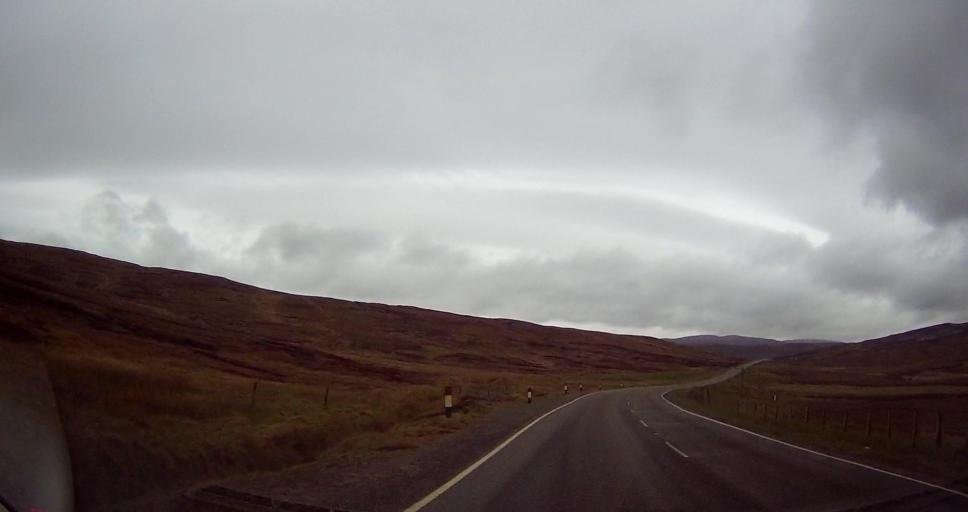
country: GB
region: Scotland
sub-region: Shetland Islands
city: Lerwick
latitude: 60.2674
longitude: -1.2294
